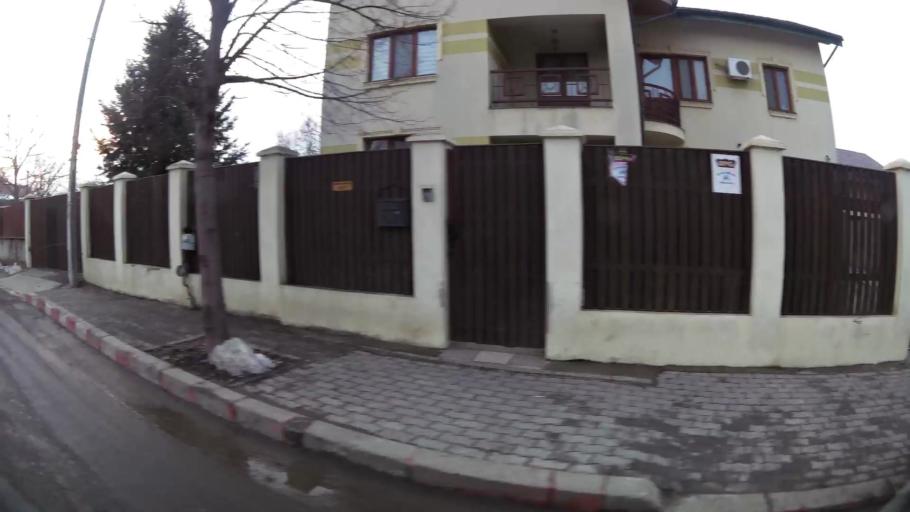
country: RO
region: Ilfov
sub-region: Voluntari City
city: Voluntari
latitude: 44.4959
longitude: 26.1673
